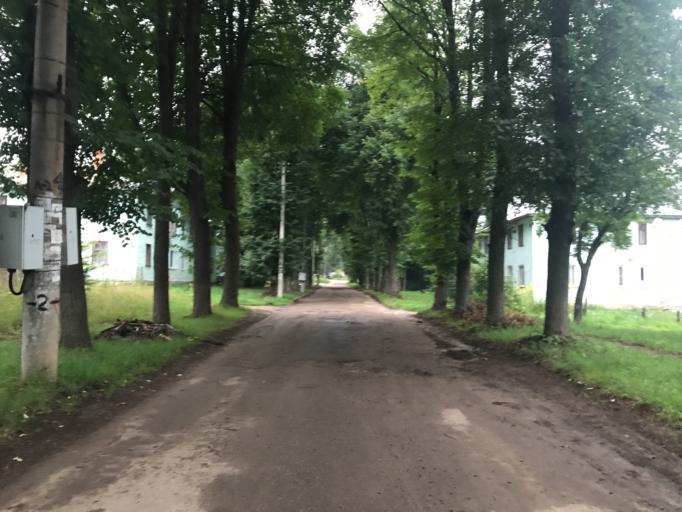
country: RU
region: Tula
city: Priupskiy
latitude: 53.9406
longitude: 37.7045
